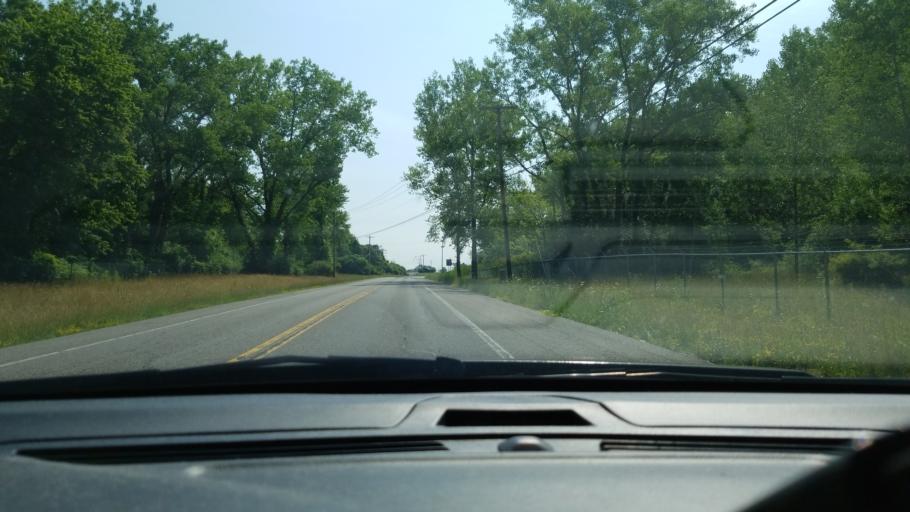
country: US
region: New York
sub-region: Onondaga County
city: Lyncourt
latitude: 43.0988
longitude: -76.1237
